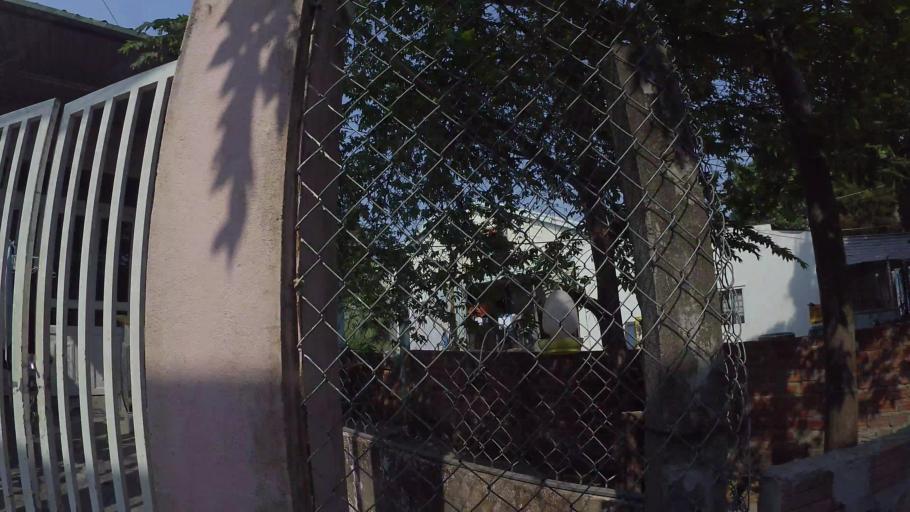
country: VN
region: Da Nang
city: Cam Le
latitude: 16.0034
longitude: 108.1923
